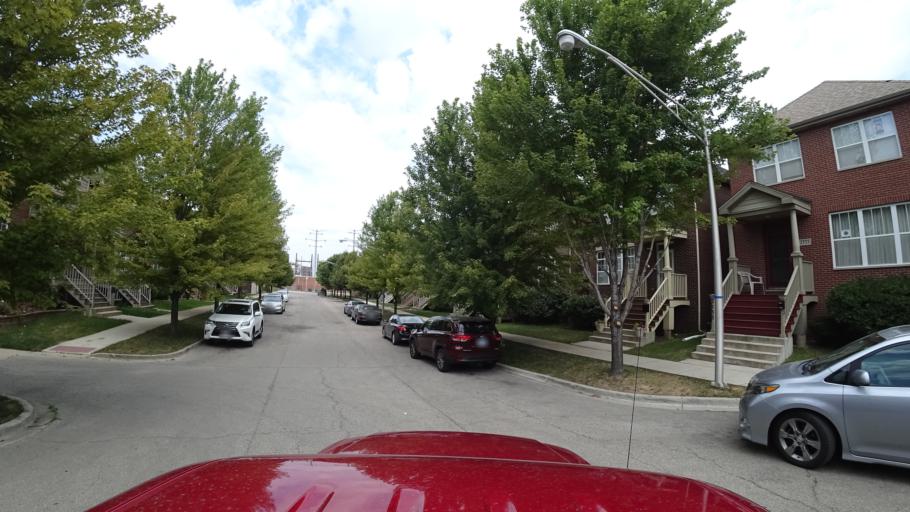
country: US
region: Illinois
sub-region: Cook County
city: Chicago
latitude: 41.8457
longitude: -87.6530
